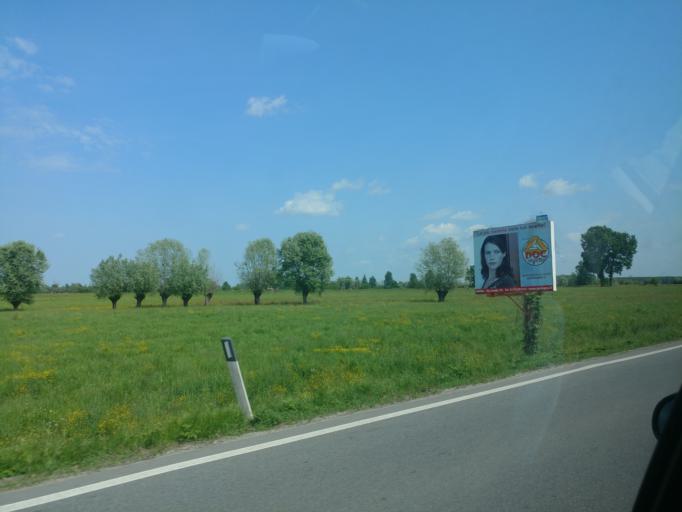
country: IT
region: Piedmont
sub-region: Provincia di Cuneo
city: Carde
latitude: 44.7246
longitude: 7.4351
